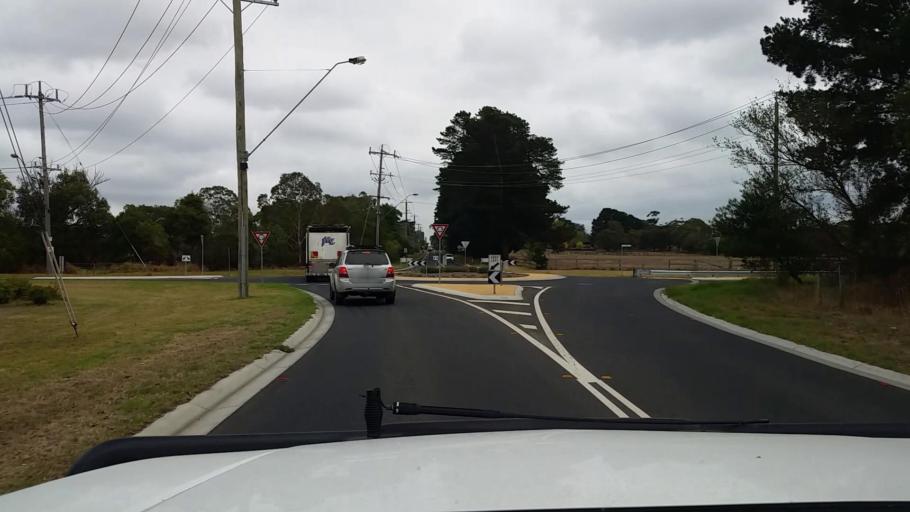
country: AU
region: Victoria
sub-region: Mornington Peninsula
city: Hastings
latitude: -38.2846
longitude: 145.1677
